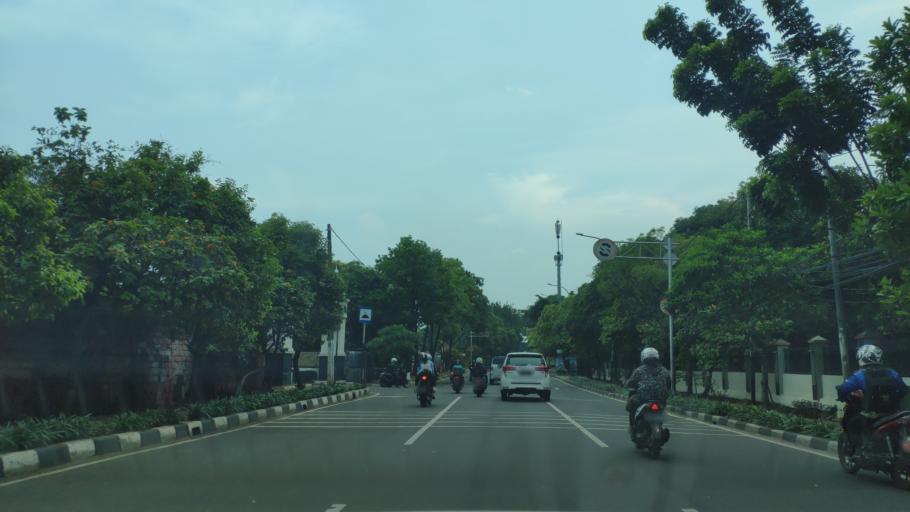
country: ID
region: Jakarta Raya
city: Jakarta
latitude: -6.1883
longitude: 106.7845
